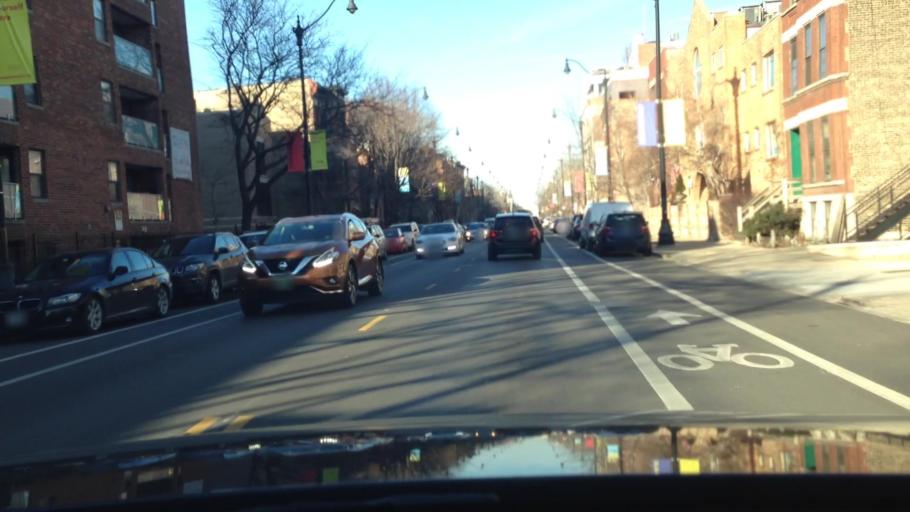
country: US
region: Illinois
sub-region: Cook County
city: Chicago
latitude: 41.9142
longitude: -87.6484
